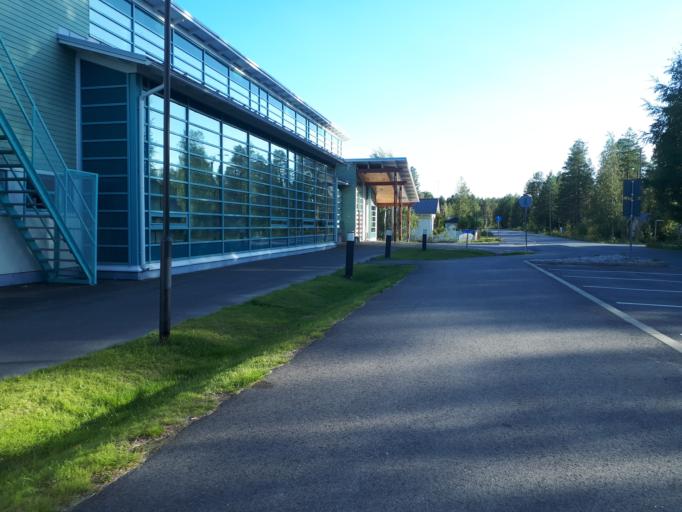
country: FI
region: Northern Ostrobothnia
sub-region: Oulunkaari
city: Ii
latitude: 65.3147
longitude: 25.3860
